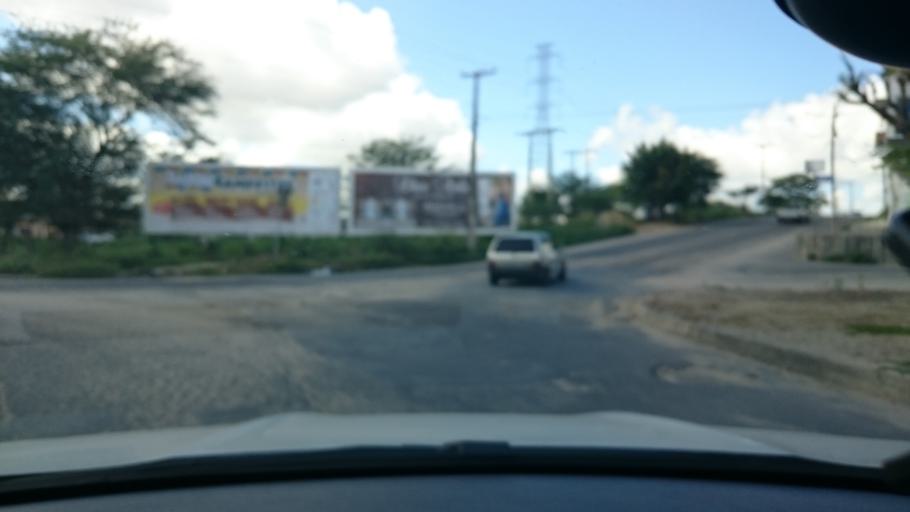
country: BR
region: Paraiba
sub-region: Campina Grande
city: Campina Grande
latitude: -7.2376
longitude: -35.9240
